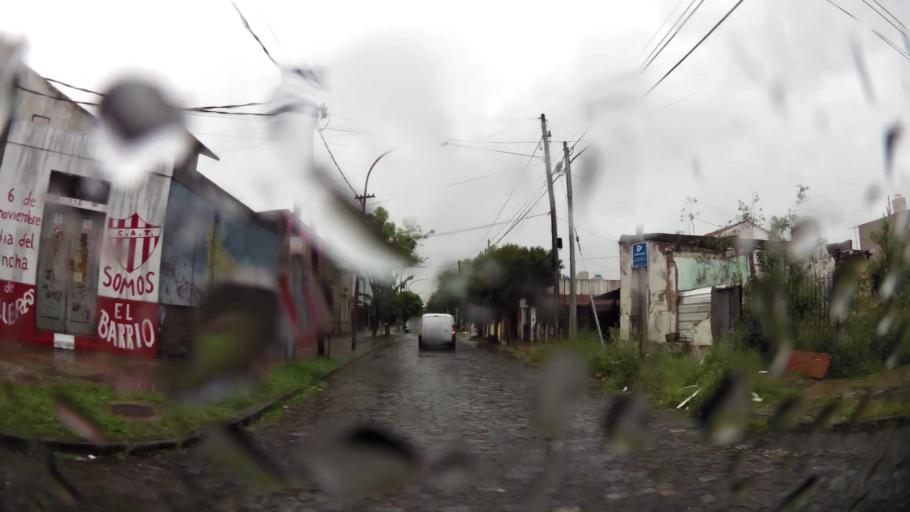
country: AR
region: Buenos Aires
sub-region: Partido de Lanus
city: Lanus
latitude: -34.7259
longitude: -58.4035
